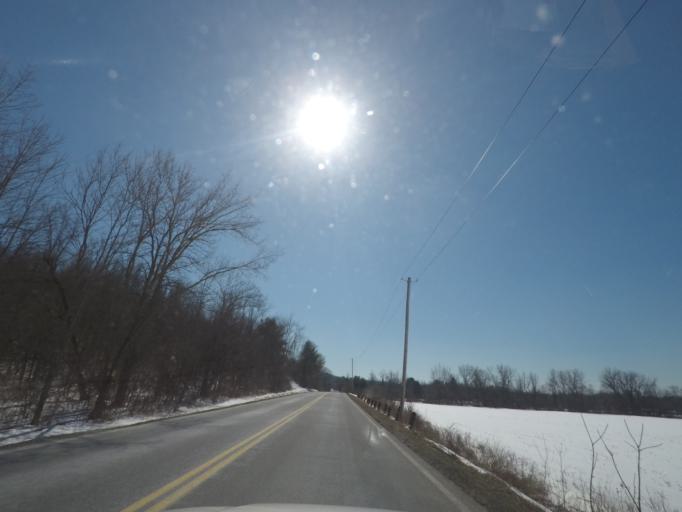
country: US
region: New York
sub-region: Saratoga County
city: Stillwater
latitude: 42.9602
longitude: -73.6231
